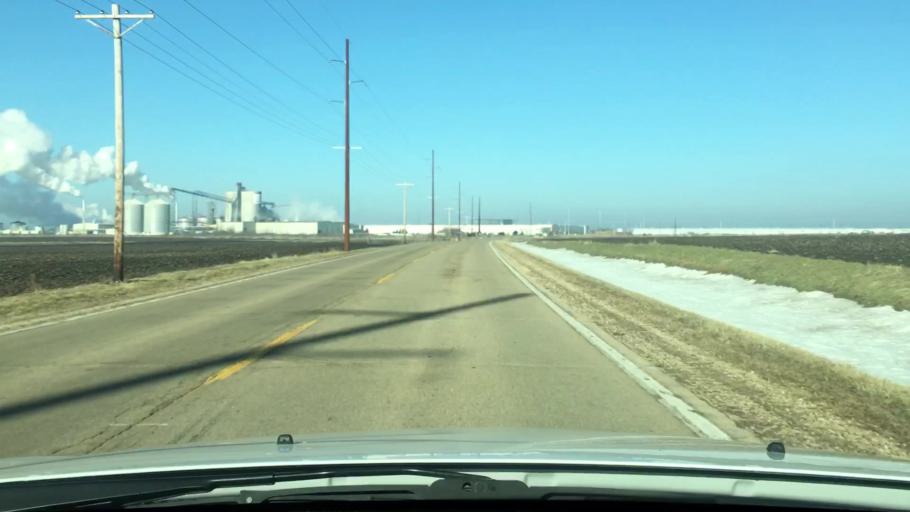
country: US
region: Illinois
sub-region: Ogle County
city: Rochelle
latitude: 41.8861
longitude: -89.0264
